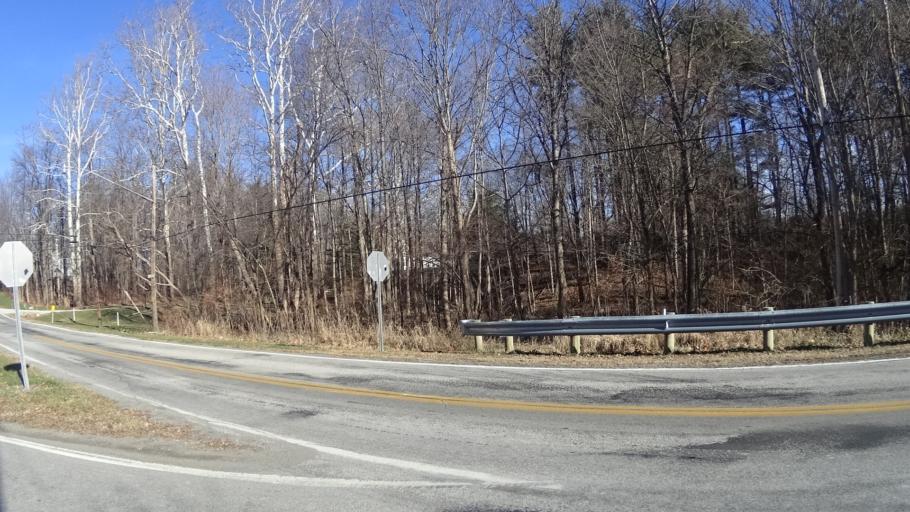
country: US
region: Ohio
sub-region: Lorain County
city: Camden
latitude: 41.2983
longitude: -82.3297
